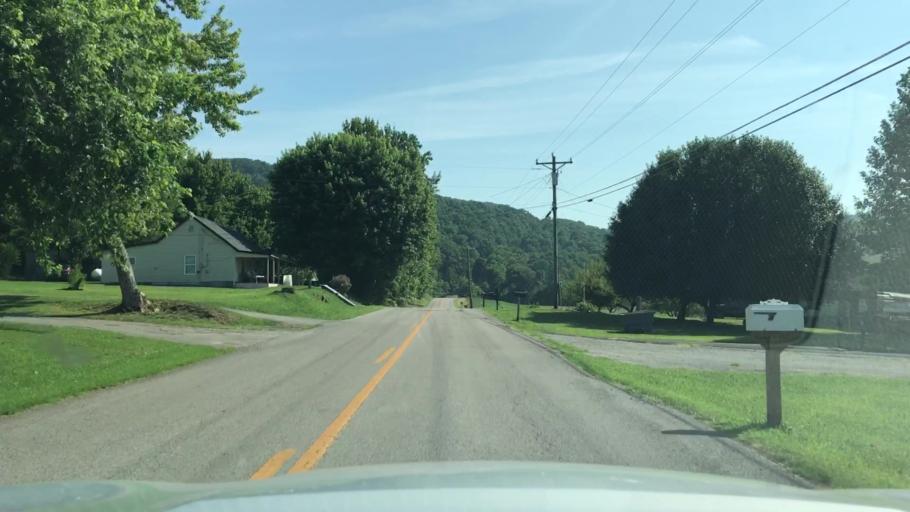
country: US
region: Kentucky
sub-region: Clinton County
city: Albany
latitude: 36.7061
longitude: -85.0347
